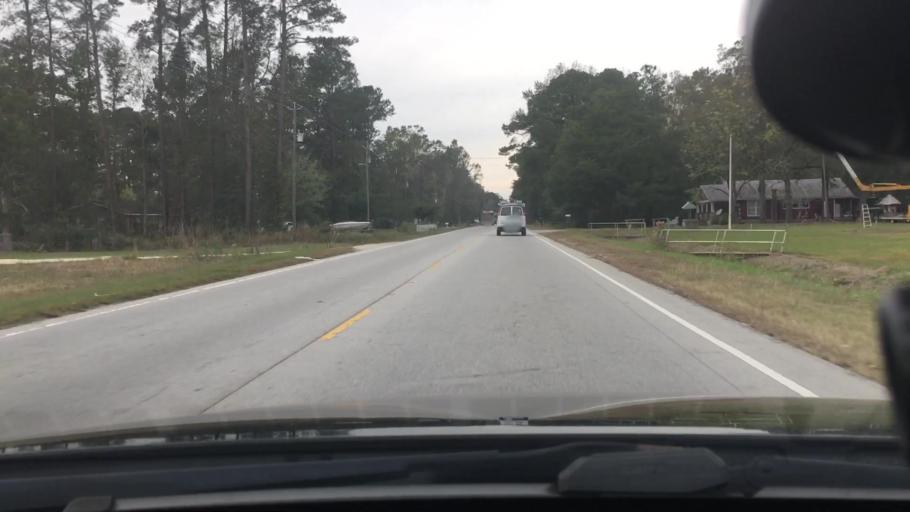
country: US
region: North Carolina
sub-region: Craven County
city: Vanceboro
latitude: 35.2580
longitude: -77.0980
